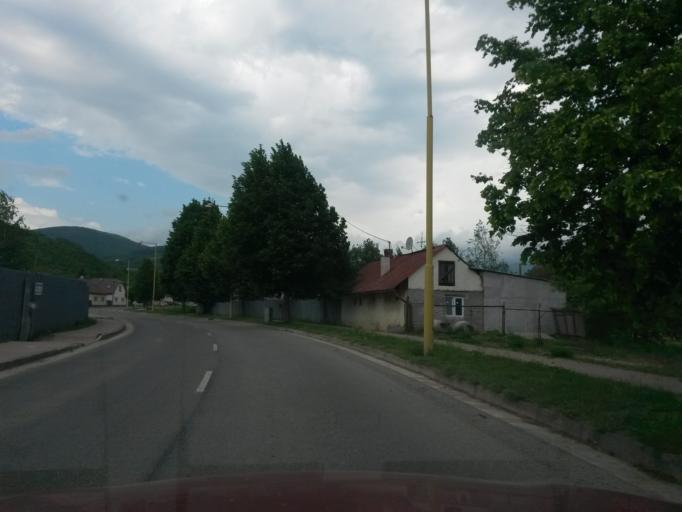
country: SK
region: Kosicky
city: Medzev
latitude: 48.6981
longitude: 20.9021
